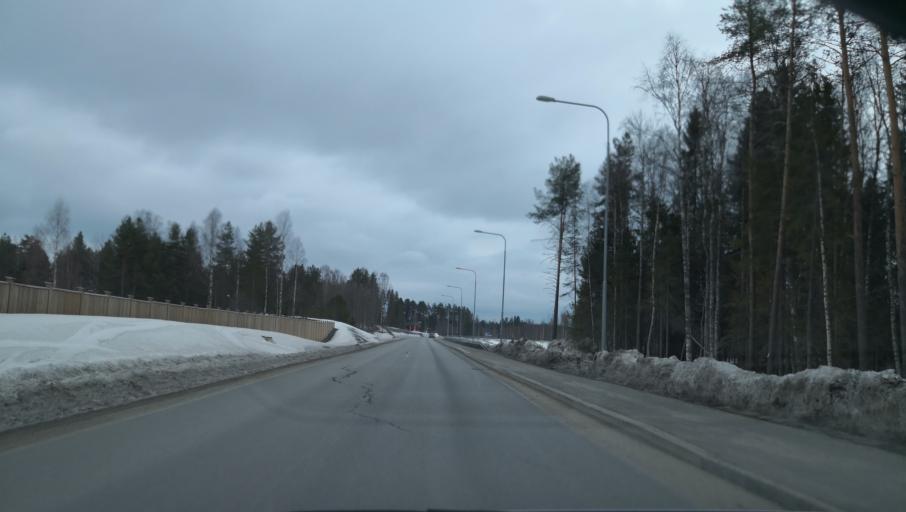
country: SE
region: Vaesterbotten
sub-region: Vannas Kommun
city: Vaennaes
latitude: 63.9114
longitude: 19.7695
